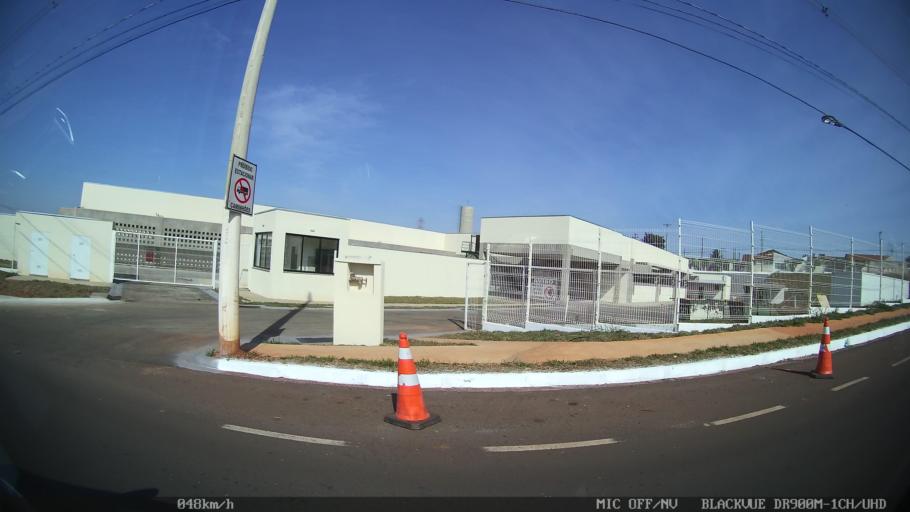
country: BR
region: Sao Paulo
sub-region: Sao Jose Do Rio Preto
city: Sao Jose do Rio Preto
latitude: -20.7893
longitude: -49.4148
